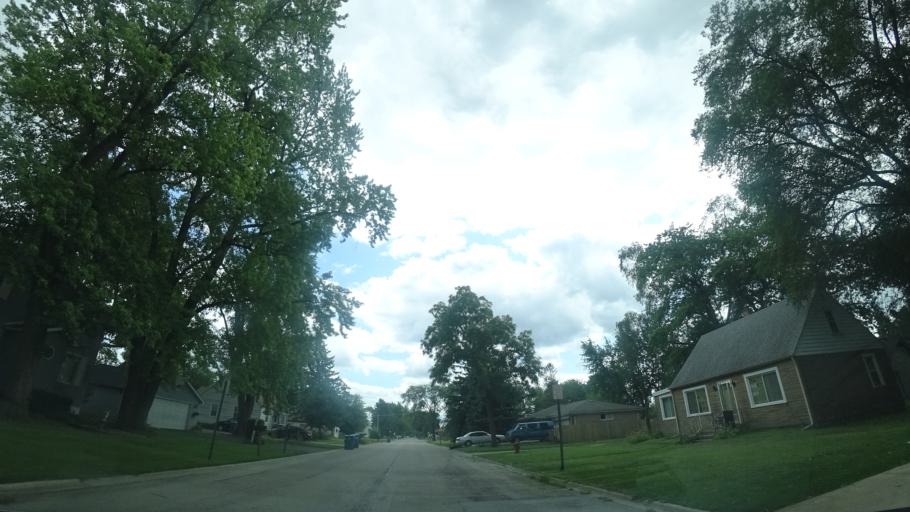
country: US
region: Illinois
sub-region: Cook County
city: Merrionette Park
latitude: 41.6816
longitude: -87.7213
